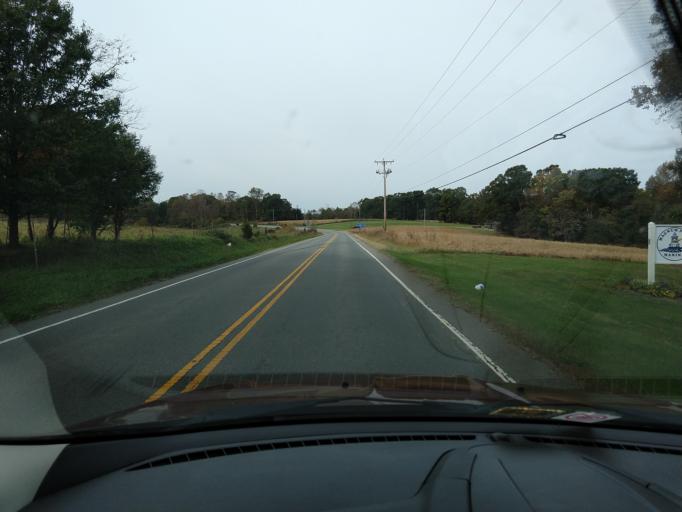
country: US
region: Virginia
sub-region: Franklin County
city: Union Hall
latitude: 36.9980
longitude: -79.6947
